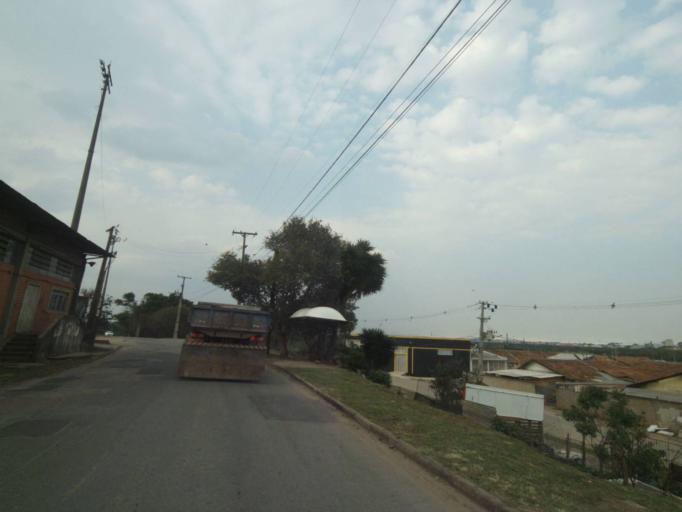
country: BR
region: Parana
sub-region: Sao Jose Dos Pinhais
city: Sao Jose dos Pinhais
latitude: -25.5329
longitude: -49.2309
